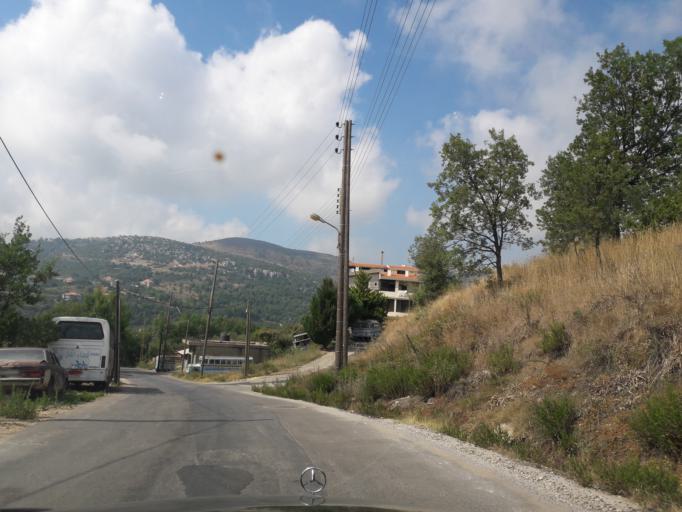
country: LB
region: Mont-Liban
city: Djounie
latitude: 33.9568
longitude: 35.7771
